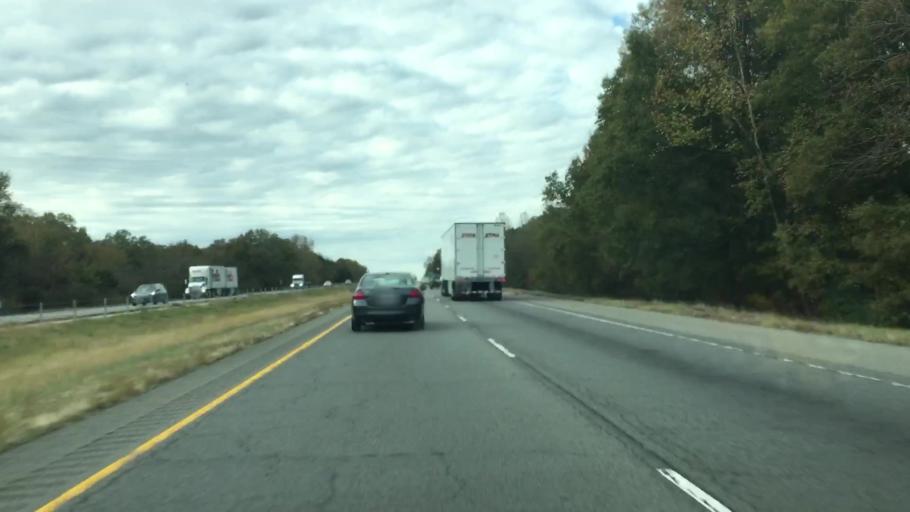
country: US
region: Arkansas
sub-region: Faulkner County
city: Conway
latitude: 35.1419
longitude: -92.5291
